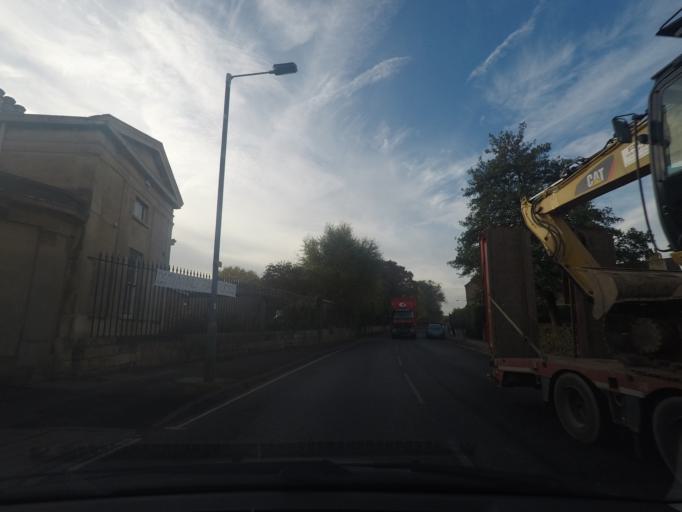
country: GB
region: England
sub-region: City of York
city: York
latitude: 53.9504
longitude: -1.0726
